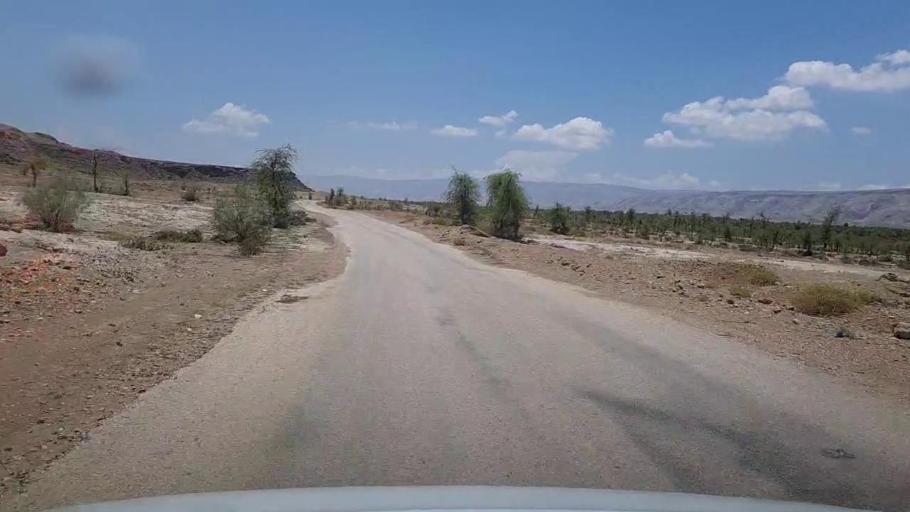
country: PK
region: Sindh
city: Bhan
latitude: 26.2981
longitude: 67.5344
